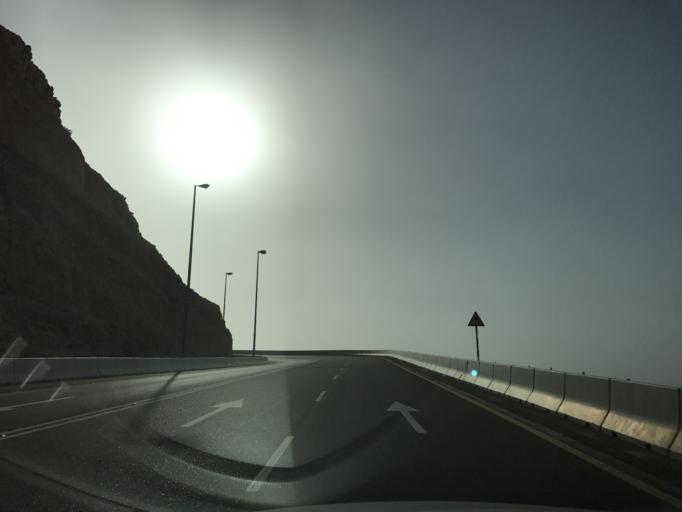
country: AE
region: Abu Dhabi
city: Al Ain
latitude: 24.0960
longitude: 55.7580
